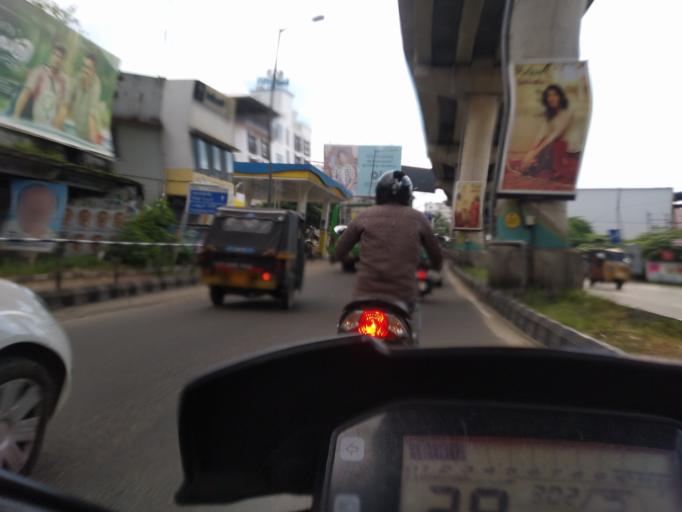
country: IN
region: Kerala
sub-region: Ernakulam
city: Cochin
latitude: 9.9878
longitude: 76.2854
